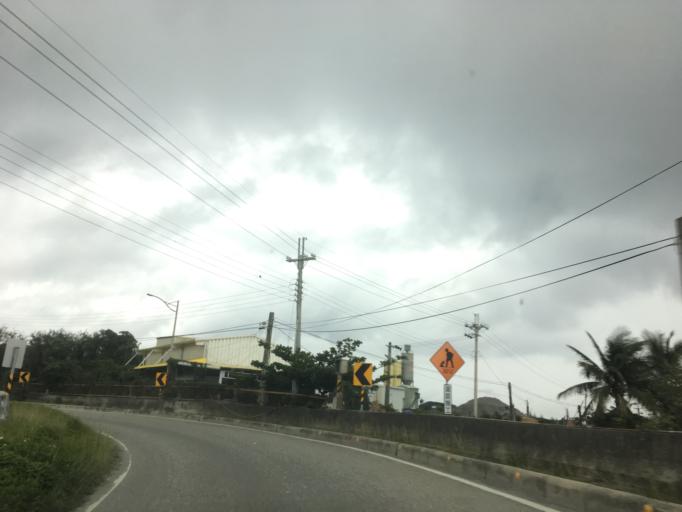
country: TW
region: Taiwan
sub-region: Taitung
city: Taitung
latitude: 22.7753
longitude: 121.1744
